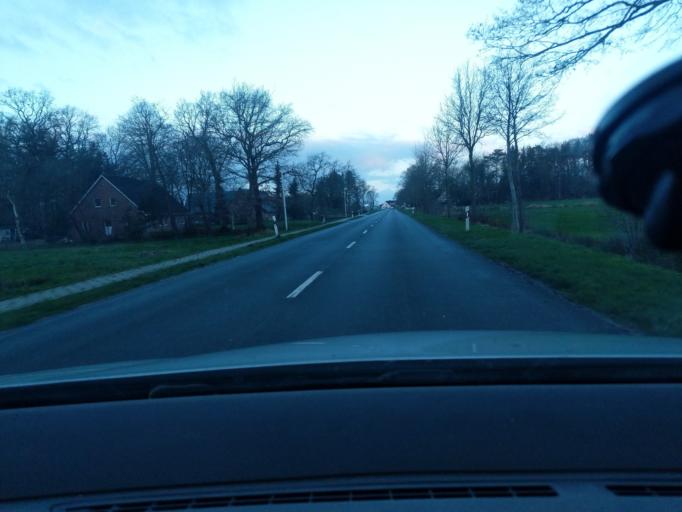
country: DE
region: Lower Saxony
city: Stinstedt
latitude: 53.6347
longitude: 8.9671
